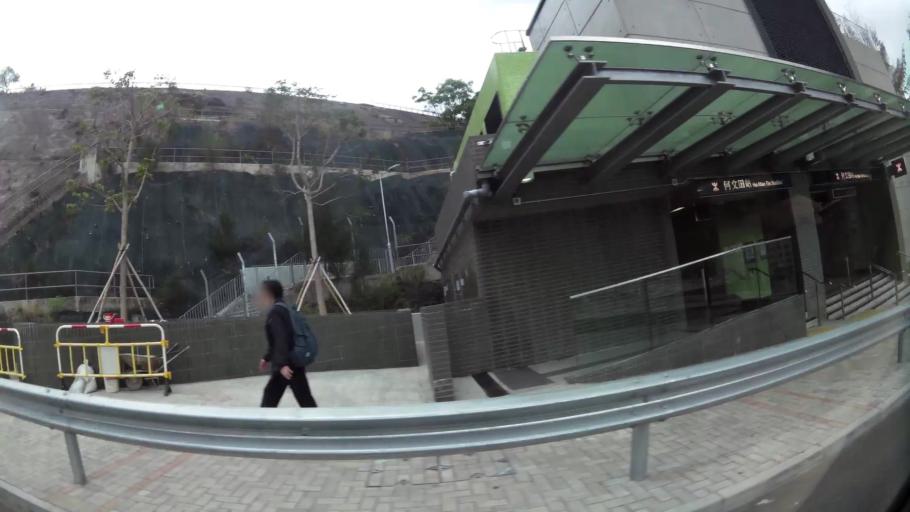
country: HK
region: Kowloon City
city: Kowloon
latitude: 22.3113
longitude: 114.1835
